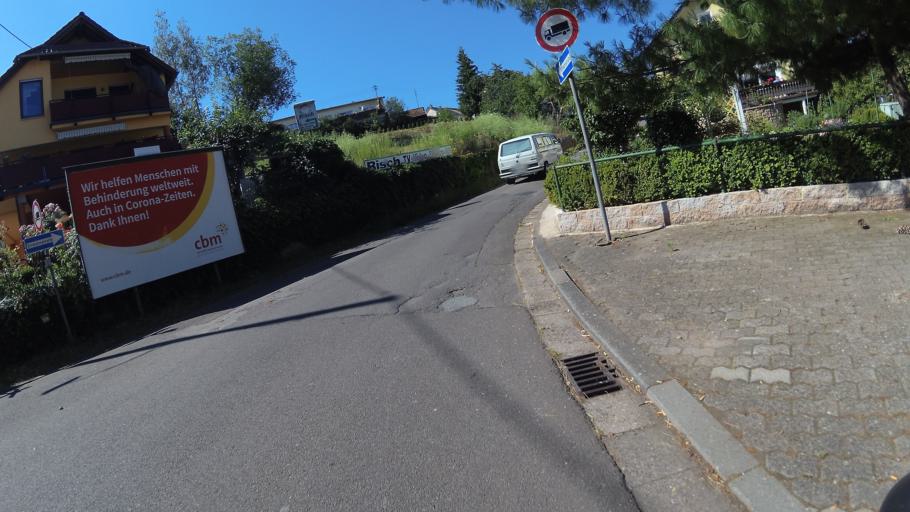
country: DE
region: Saarland
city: Schmelz
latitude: 49.4760
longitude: 6.8982
